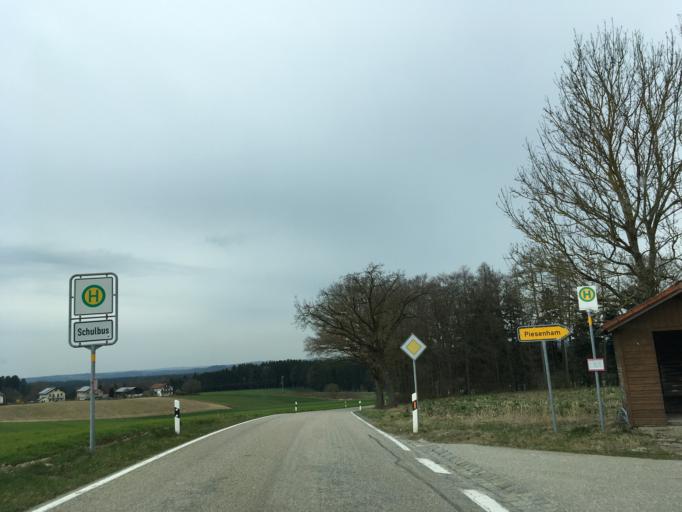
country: DE
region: Bavaria
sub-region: Upper Bavaria
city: Jettenbach
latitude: 48.1463
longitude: 12.3883
